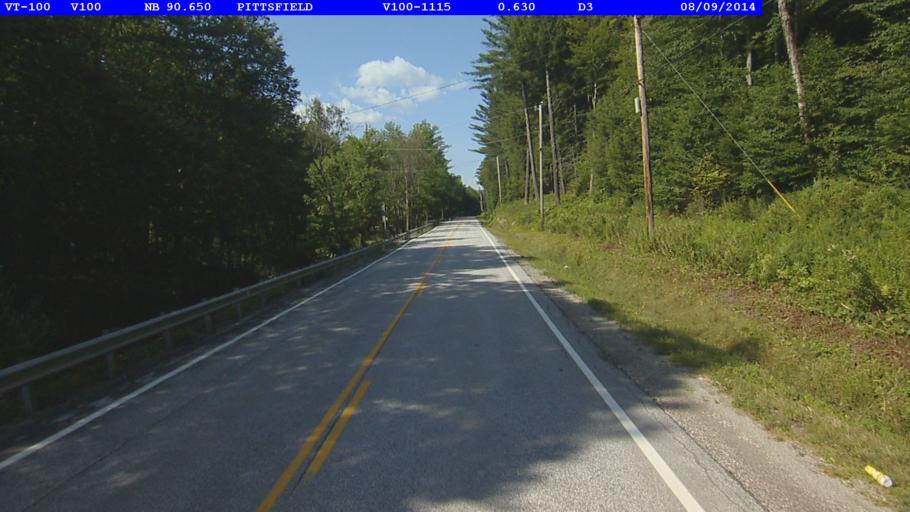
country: US
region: Vermont
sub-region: Rutland County
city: Rutland
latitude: 43.7264
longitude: -72.8230
